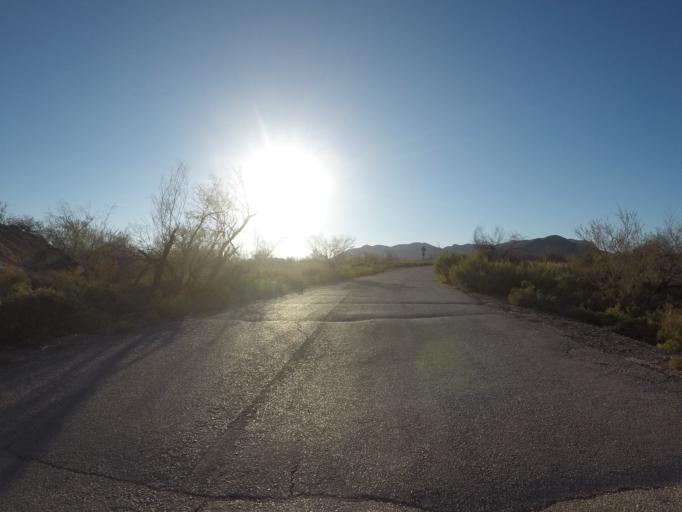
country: US
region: Nevada
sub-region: Clark County
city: Moapa Valley
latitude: 36.3895
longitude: -114.4199
